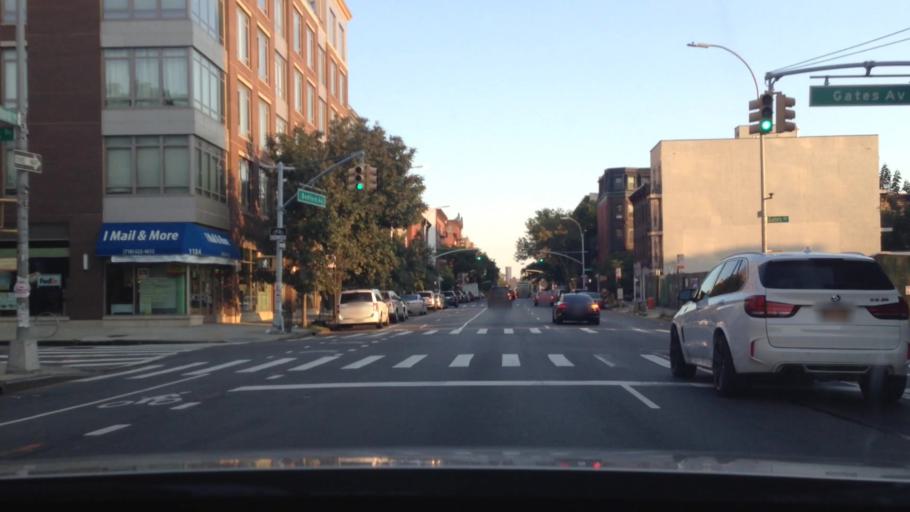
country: US
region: New York
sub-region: Kings County
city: Brooklyn
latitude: 40.6856
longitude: -73.9544
